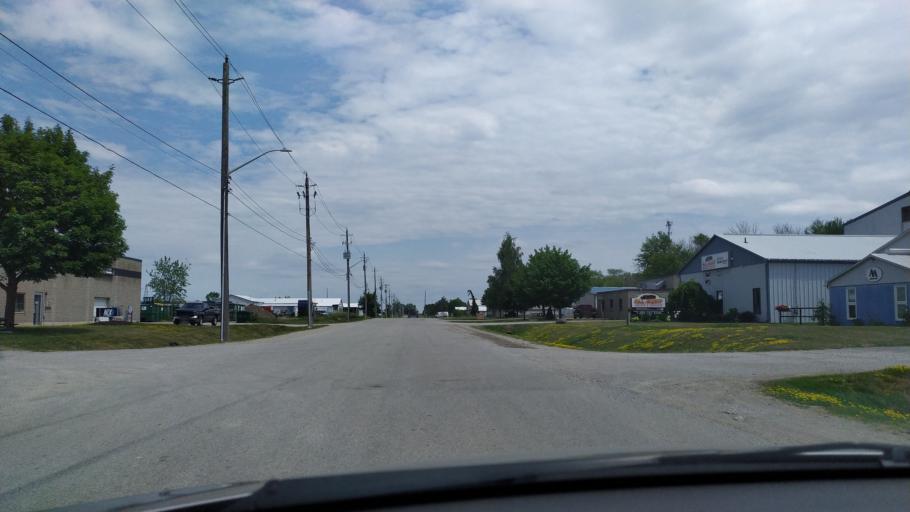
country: CA
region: Ontario
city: Stratford
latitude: 43.3517
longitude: -80.9861
